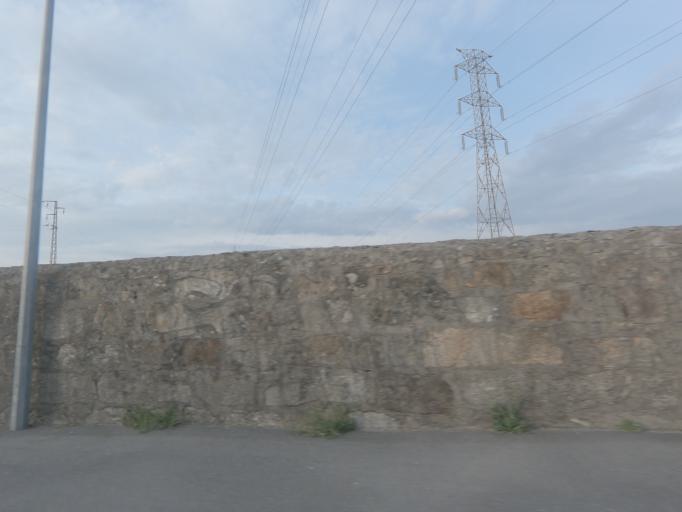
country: PT
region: Porto
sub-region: Maia
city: Leca do Bailio
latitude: 41.2056
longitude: -8.6200
